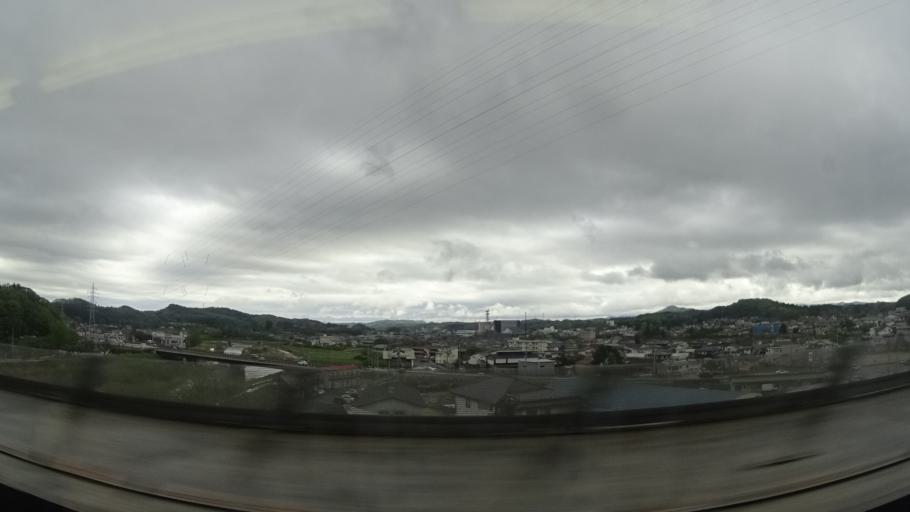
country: JP
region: Tochigi
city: Kuroiso
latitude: 37.1362
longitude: 140.2011
